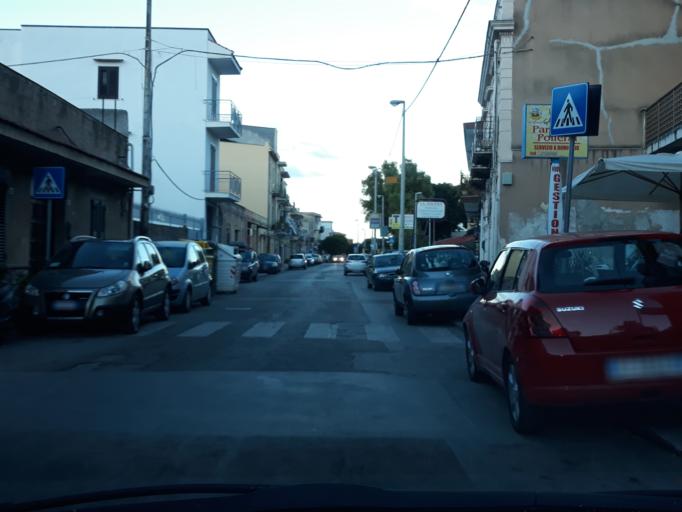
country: IT
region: Sicily
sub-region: Palermo
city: Villa Ciambra
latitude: 38.0898
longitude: 13.3304
